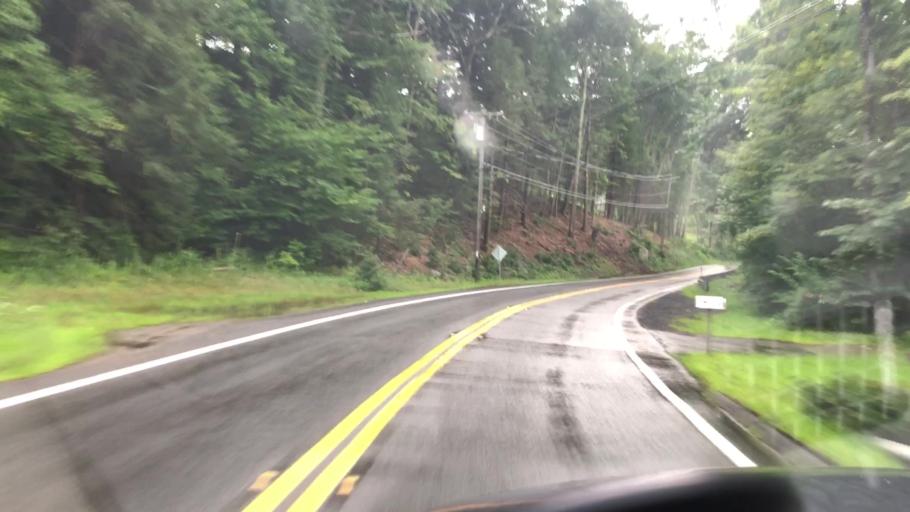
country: US
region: Massachusetts
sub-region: Hampshire County
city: Westhampton
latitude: 42.2609
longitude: -72.8638
